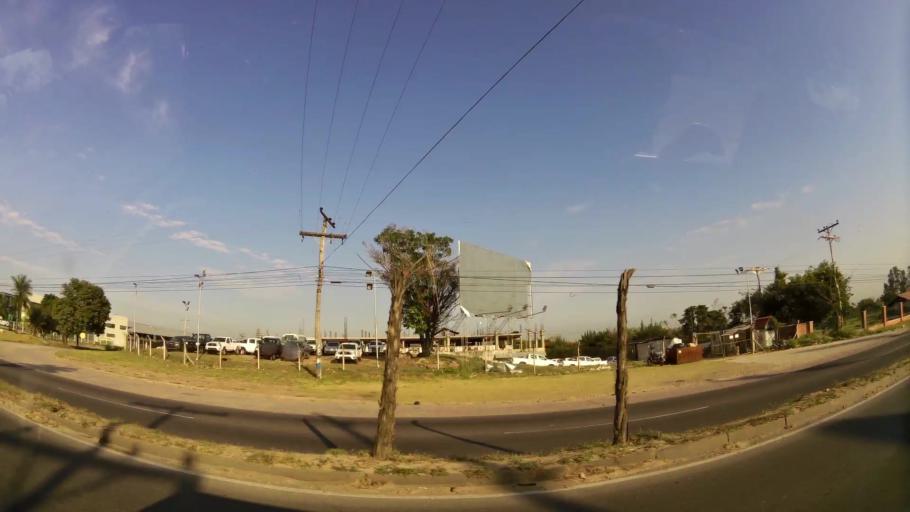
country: BO
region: Santa Cruz
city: Santa Cruz de la Sierra
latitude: -17.6836
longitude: -63.1590
